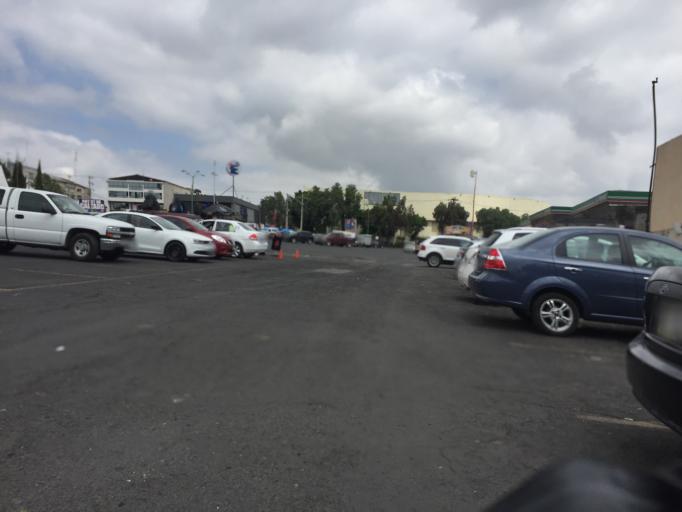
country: MX
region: Mexico
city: Cuautitlan Izcalli
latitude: 19.6514
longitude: -99.2054
